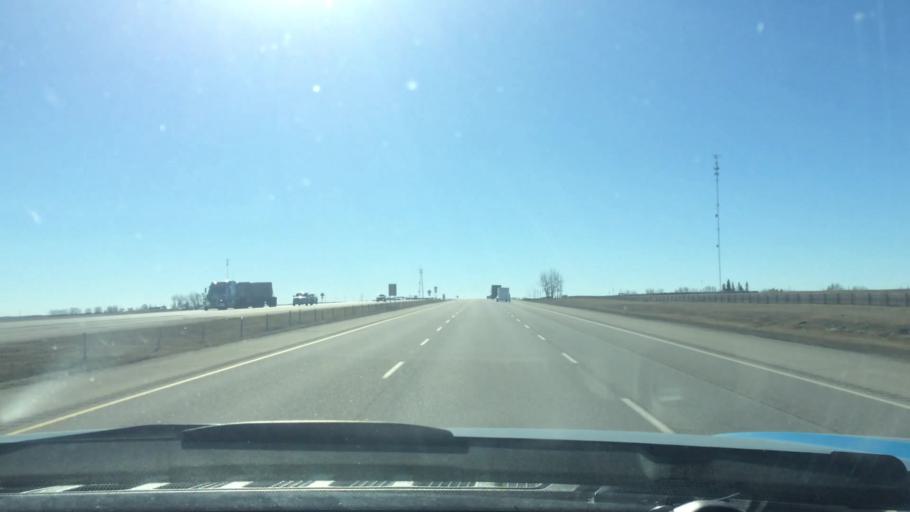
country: CA
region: Alberta
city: Crossfield
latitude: 51.4250
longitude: -114.0021
